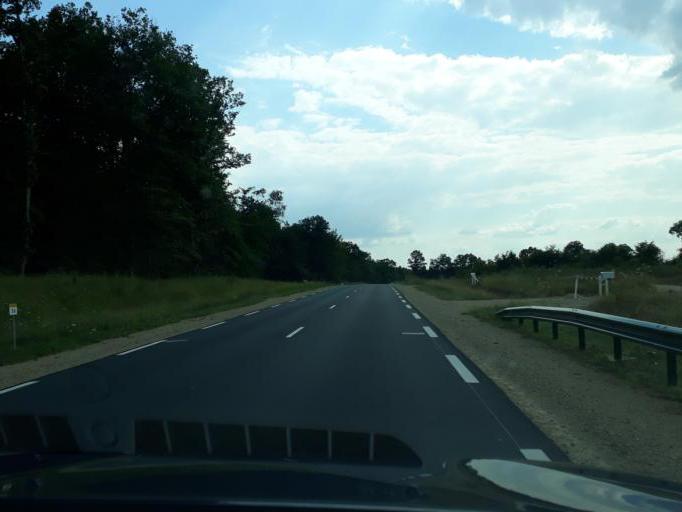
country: FR
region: Centre
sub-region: Departement du Cher
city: Cours-les-Barres
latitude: 46.9924
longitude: 3.0062
